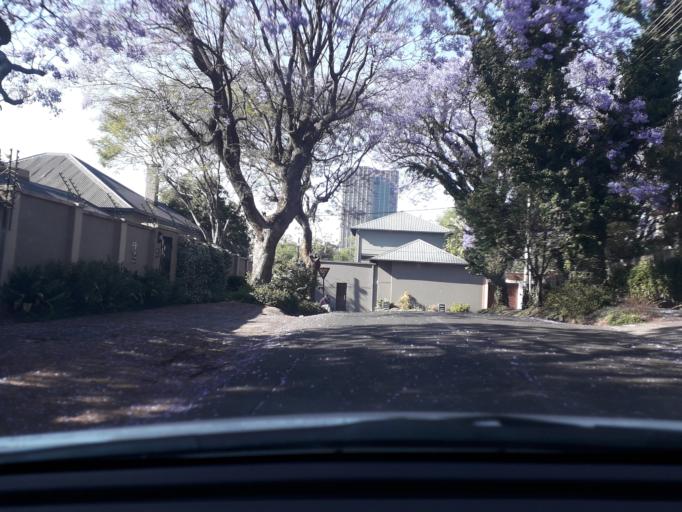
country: ZA
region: Gauteng
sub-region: City of Johannesburg Metropolitan Municipality
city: Johannesburg
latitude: -26.1780
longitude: 28.0126
